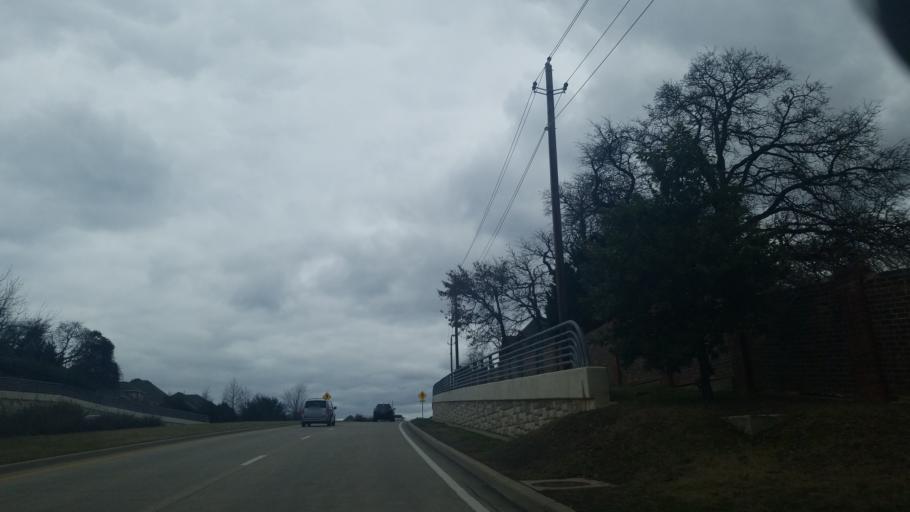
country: US
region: Texas
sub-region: Denton County
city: Copper Canyon
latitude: 33.0950
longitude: -97.0803
